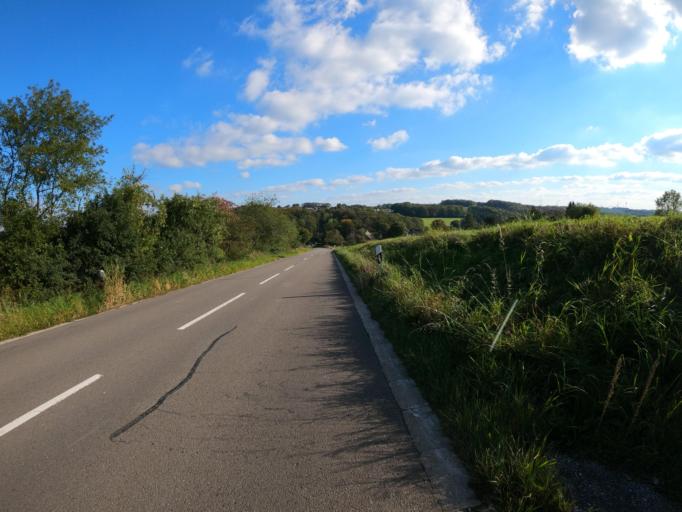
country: DE
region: North Rhine-Westphalia
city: Radevormwald
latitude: 51.2281
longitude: 7.3422
